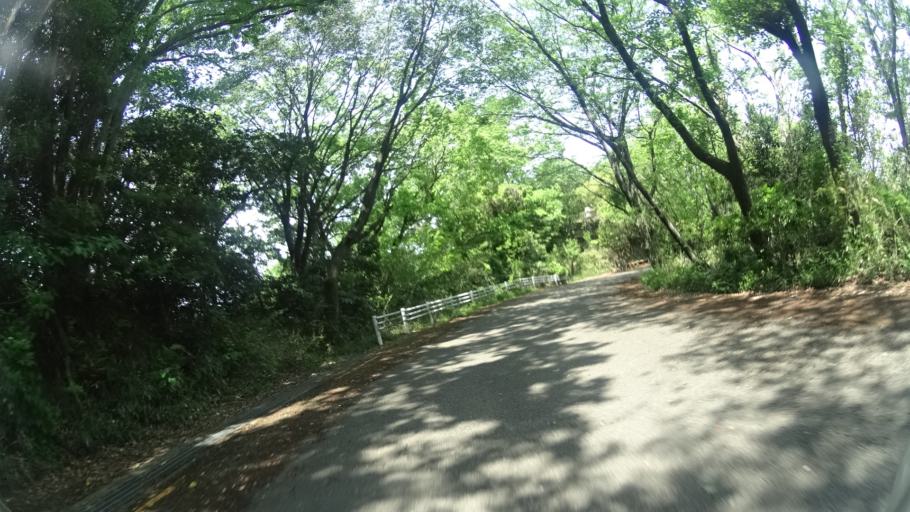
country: JP
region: Tokushima
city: Tokushima-shi
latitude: 34.0669
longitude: 134.5185
